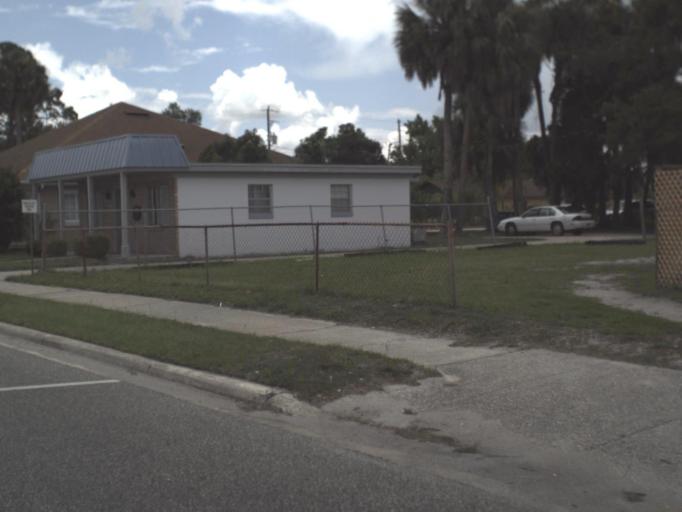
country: US
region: Florida
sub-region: Putnam County
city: Palatka
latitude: 29.6493
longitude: -81.6429
